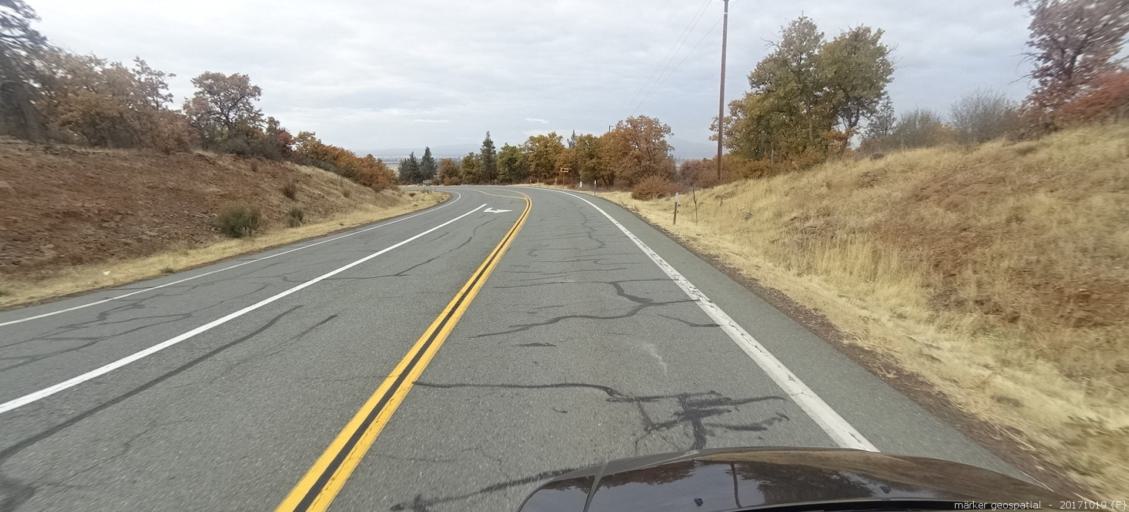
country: US
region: California
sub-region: Shasta County
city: Burney
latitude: 41.0874
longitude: -121.3159
